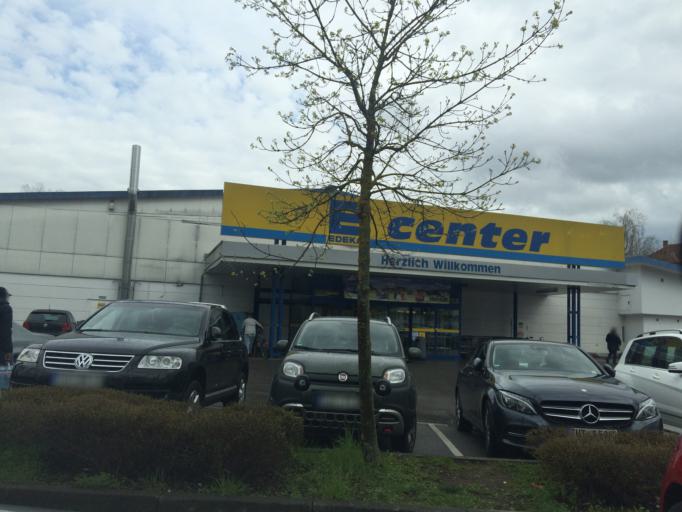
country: DE
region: Baden-Wuerttemberg
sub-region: Freiburg Region
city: Tuttlingen
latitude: 47.9836
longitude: 8.8037
